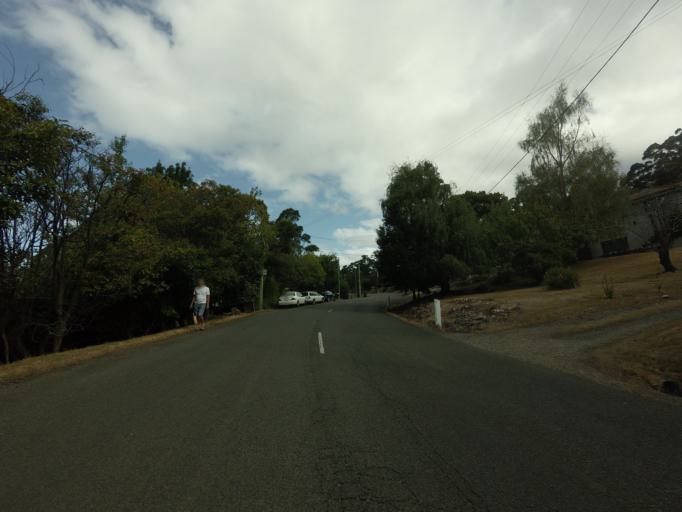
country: AU
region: Tasmania
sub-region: Hobart
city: Dynnyrne
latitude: -42.9018
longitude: 147.2704
